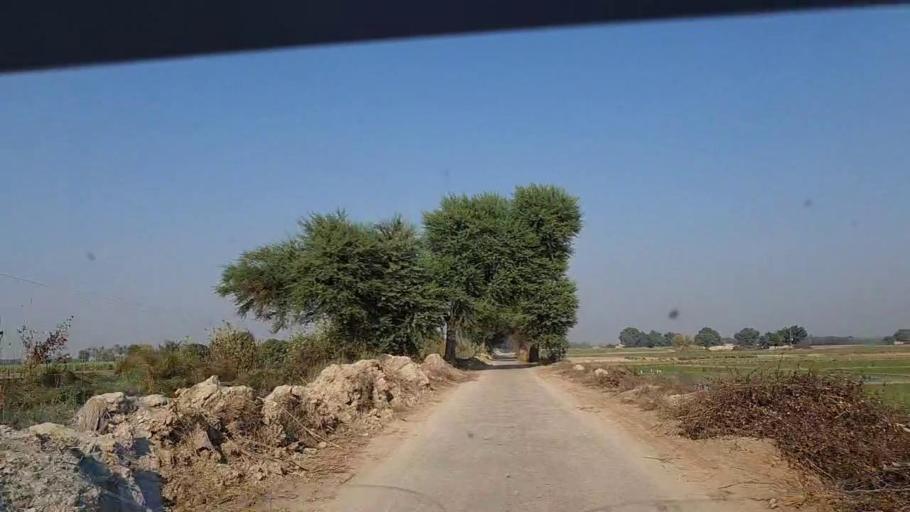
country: PK
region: Sindh
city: Hingorja
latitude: 27.2395
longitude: 68.3205
